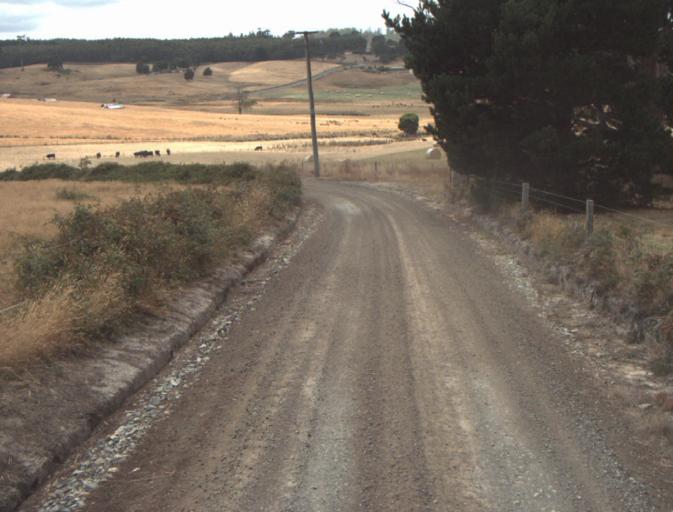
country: AU
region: Tasmania
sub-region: Launceston
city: Mayfield
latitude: -41.1984
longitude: 147.1688
